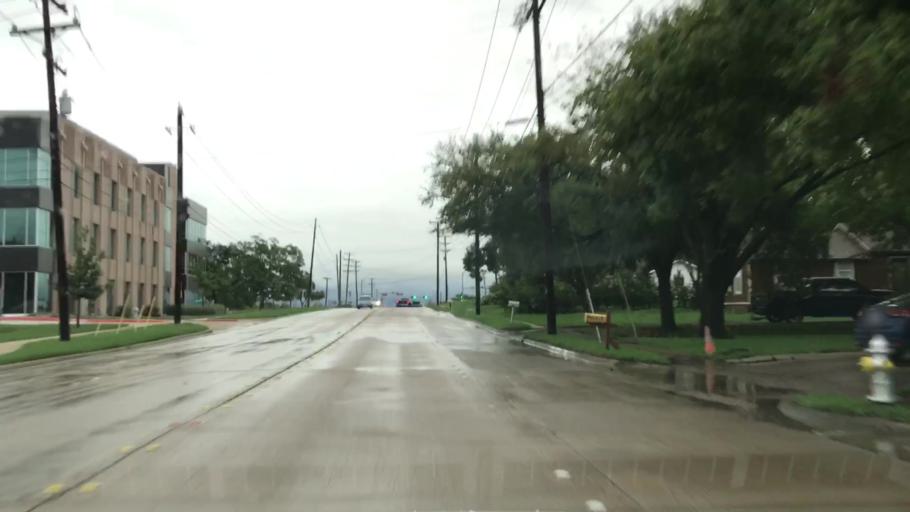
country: US
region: Texas
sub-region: Collin County
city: Wylie
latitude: 33.0172
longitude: -96.5343
